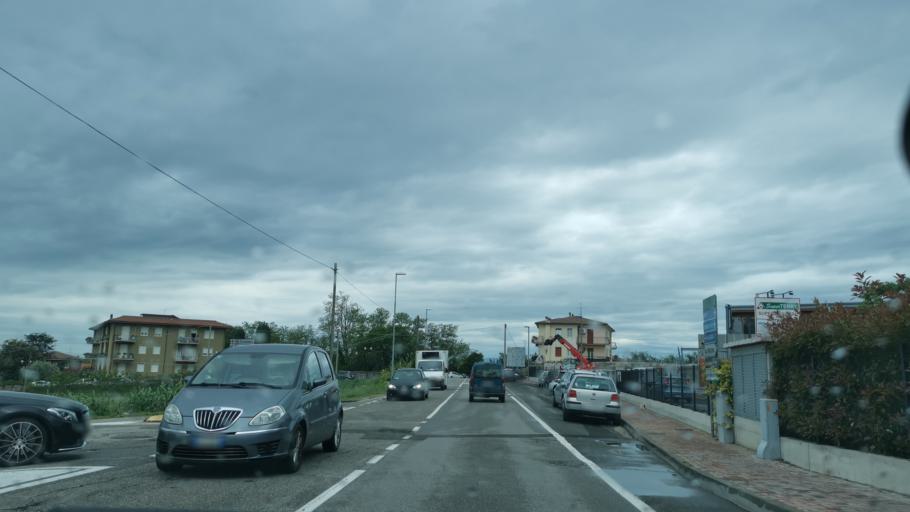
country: IT
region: Veneto
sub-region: Provincia di Verona
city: Bardolino
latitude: 45.5469
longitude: 10.7282
